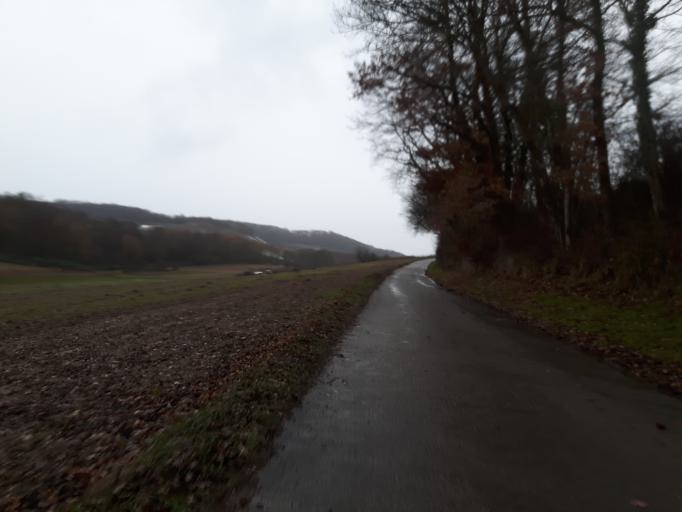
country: DE
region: Baden-Wuerttemberg
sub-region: Regierungsbezirk Stuttgart
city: Erlenbach
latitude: 49.1648
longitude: 9.2578
